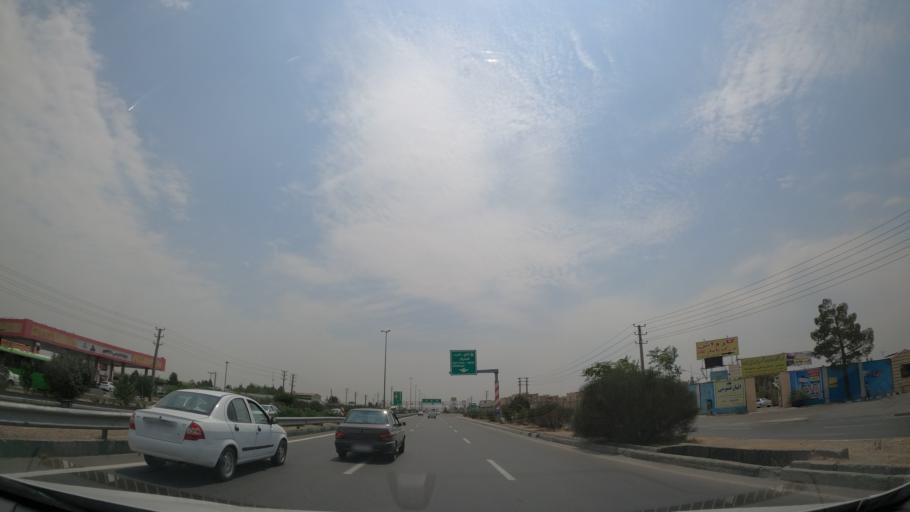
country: IR
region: Tehran
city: Shahr-e Qods
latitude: 35.6980
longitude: 51.1968
